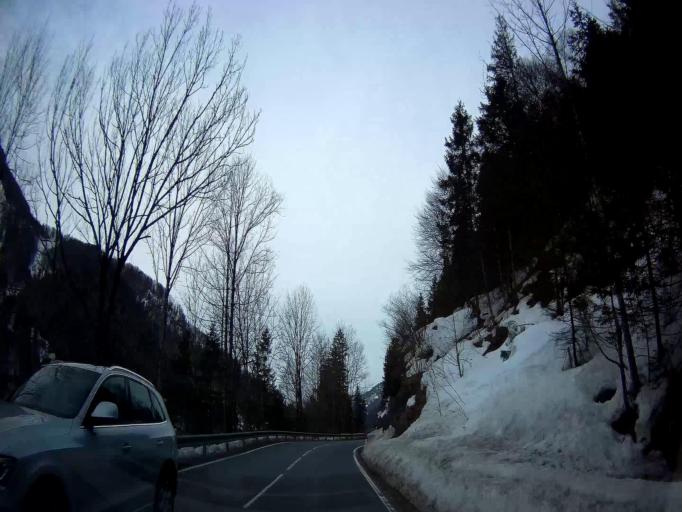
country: AT
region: Salzburg
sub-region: Politischer Bezirk Hallein
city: Krispl
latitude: 47.7513
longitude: 13.1751
